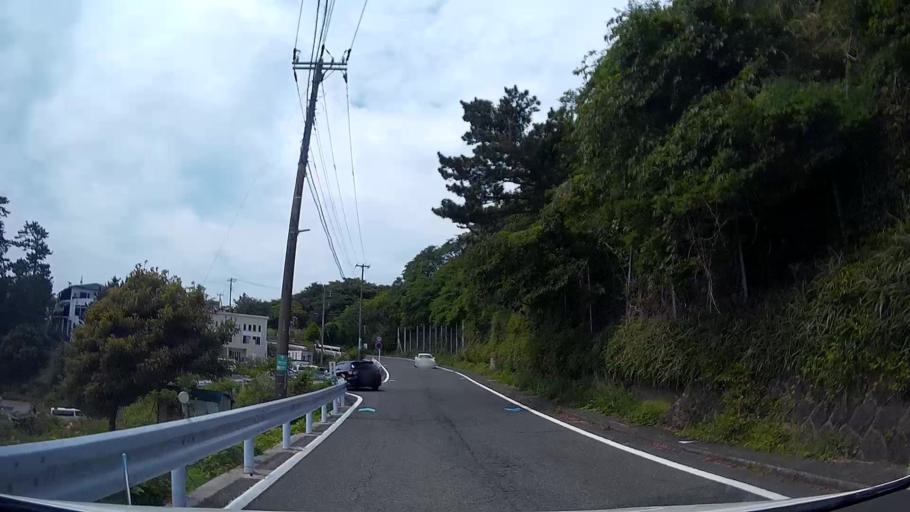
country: JP
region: Shizuoka
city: Ito
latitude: 34.8991
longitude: 139.1315
